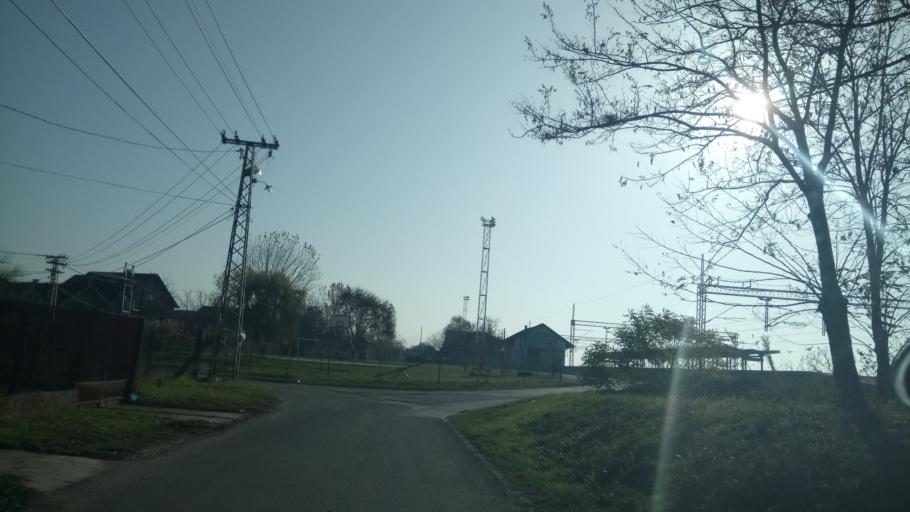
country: RS
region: Autonomna Pokrajina Vojvodina
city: Nova Pazova
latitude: 44.9389
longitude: 20.2086
